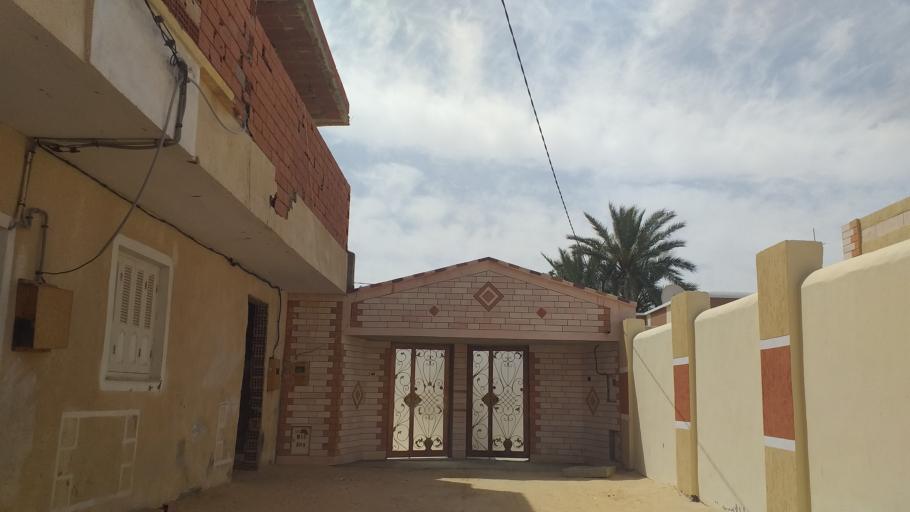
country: TN
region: Qabis
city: Gabes
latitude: 33.9483
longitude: 10.0658
